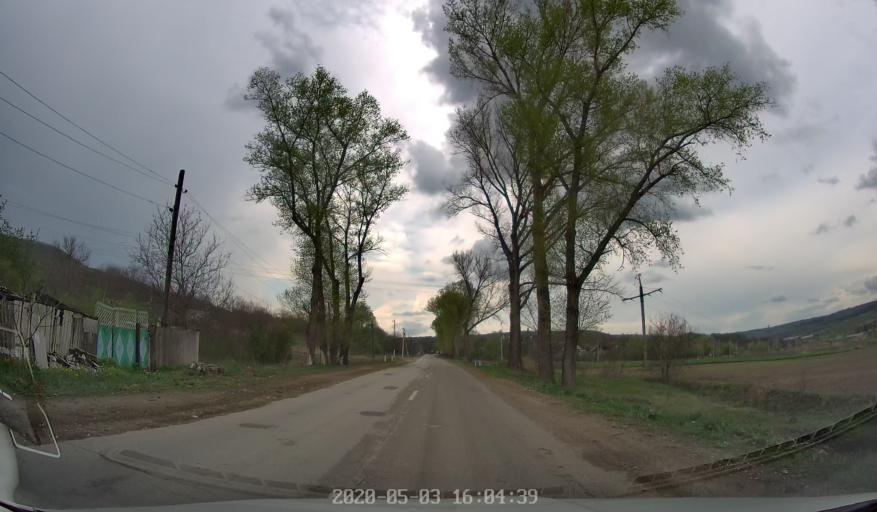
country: MD
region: Calarasi
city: Calarasi
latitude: 47.1875
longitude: 28.3646
